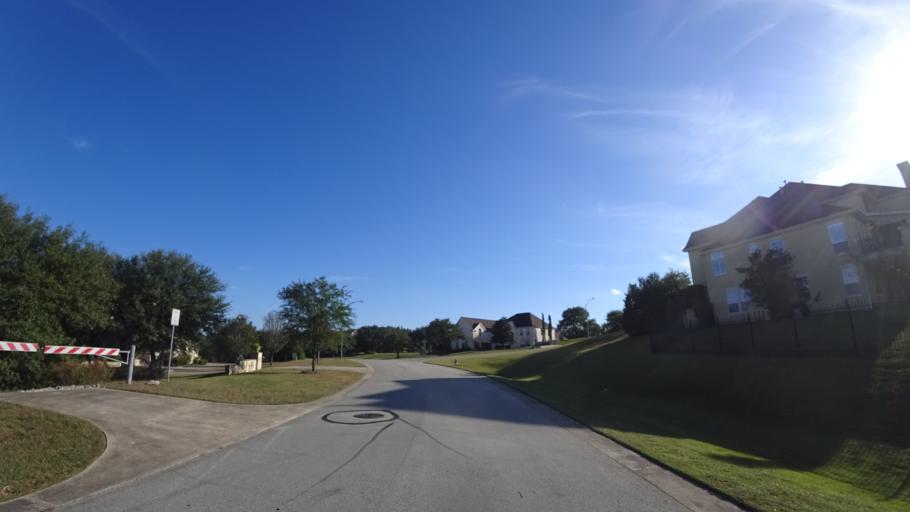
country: US
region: Texas
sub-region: Travis County
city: Barton Creek
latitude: 30.2597
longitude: -97.8442
